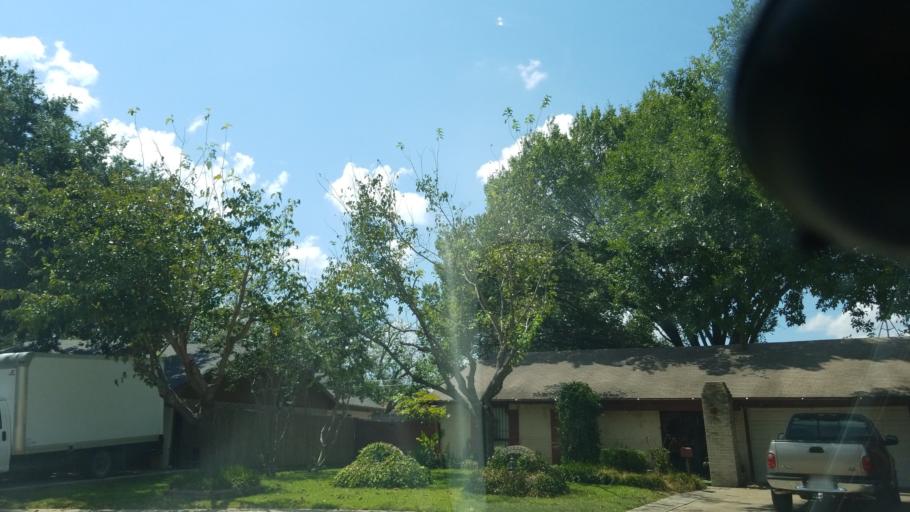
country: US
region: Texas
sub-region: Dallas County
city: Grand Prairie
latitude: 32.7233
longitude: -96.9976
